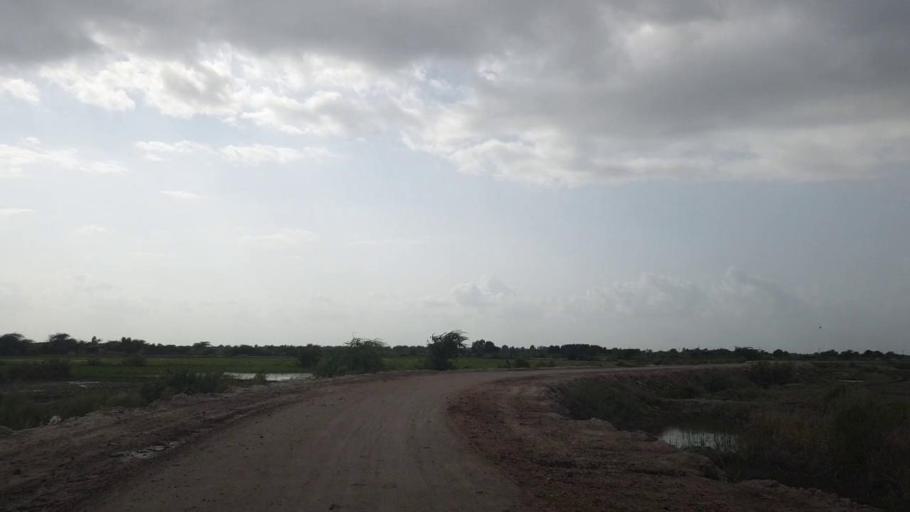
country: PK
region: Sindh
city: Kadhan
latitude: 24.5817
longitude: 69.0575
